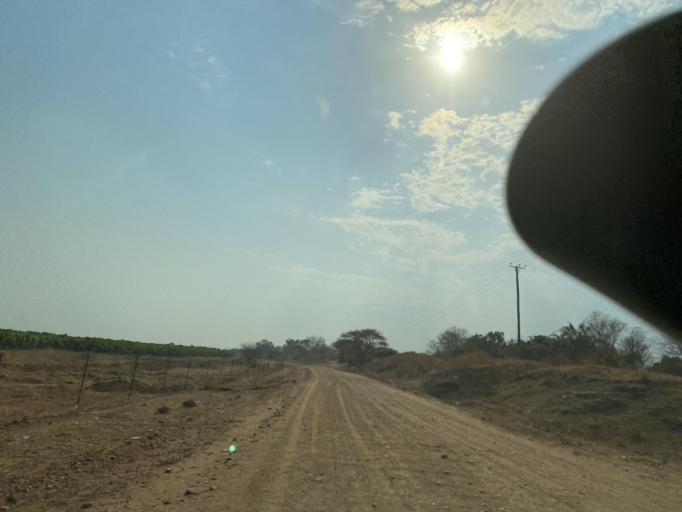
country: ZW
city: Chirundu
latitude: -15.9312
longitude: 28.9547
